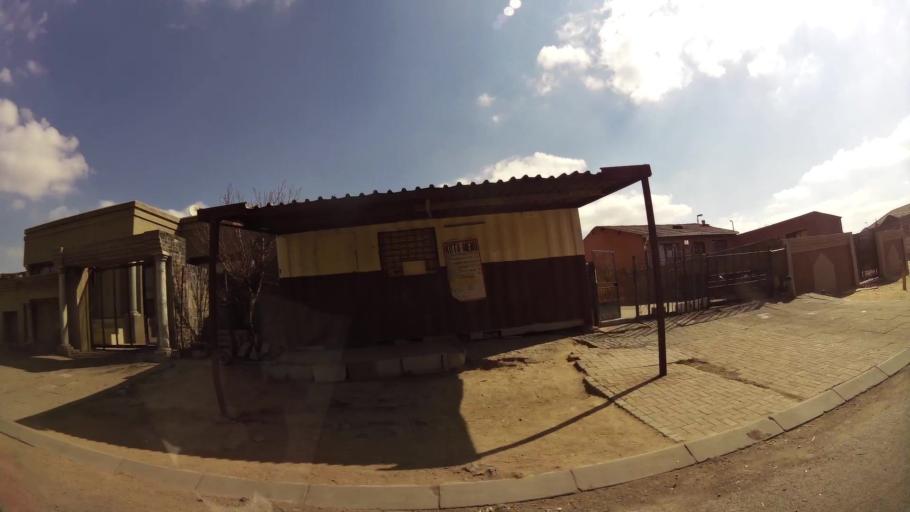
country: ZA
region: Gauteng
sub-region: Ekurhuleni Metropolitan Municipality
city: Tembisa
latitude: -26.0157
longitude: 28.2002
